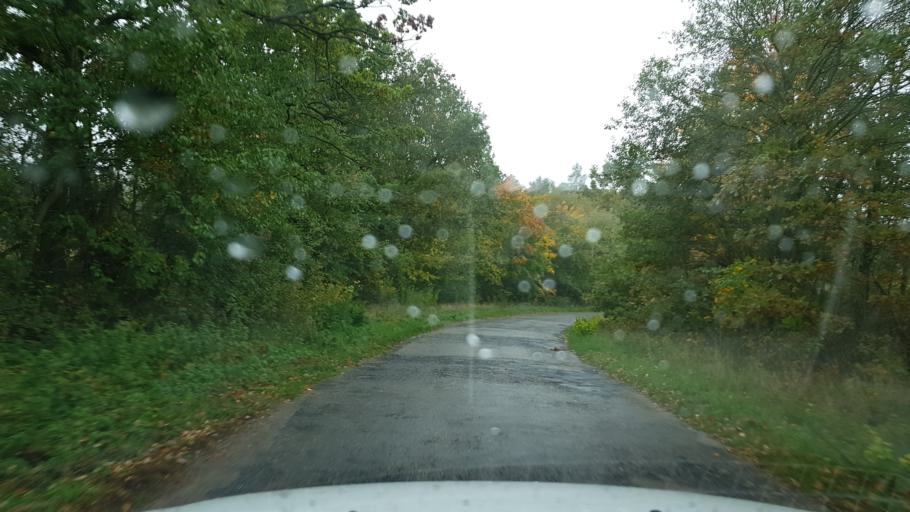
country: PL
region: West Pomeranian Voivodeship
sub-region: Powiat mysliborski
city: Barlinek
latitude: 53.0373
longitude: 15.2389
